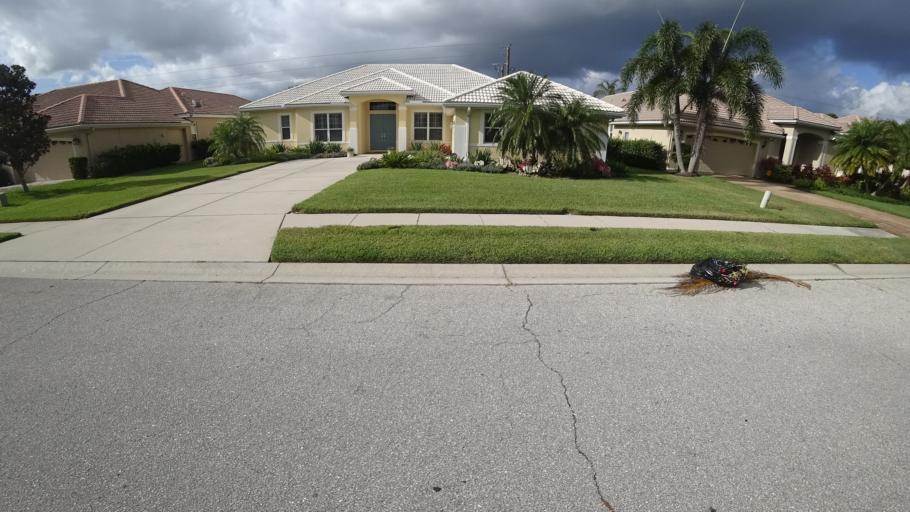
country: US
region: Florida
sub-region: Sarasota County
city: Desoto Lakes
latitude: 27.4111
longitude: -82.4832
